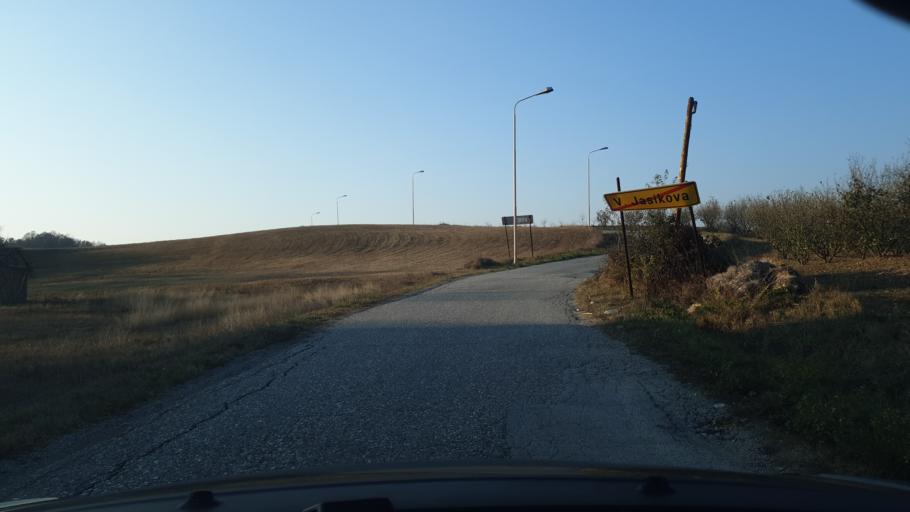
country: RS
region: Central Serbia
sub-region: Zajecarski Okrug
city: Zajecar
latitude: 44.0891
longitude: 22.3489
